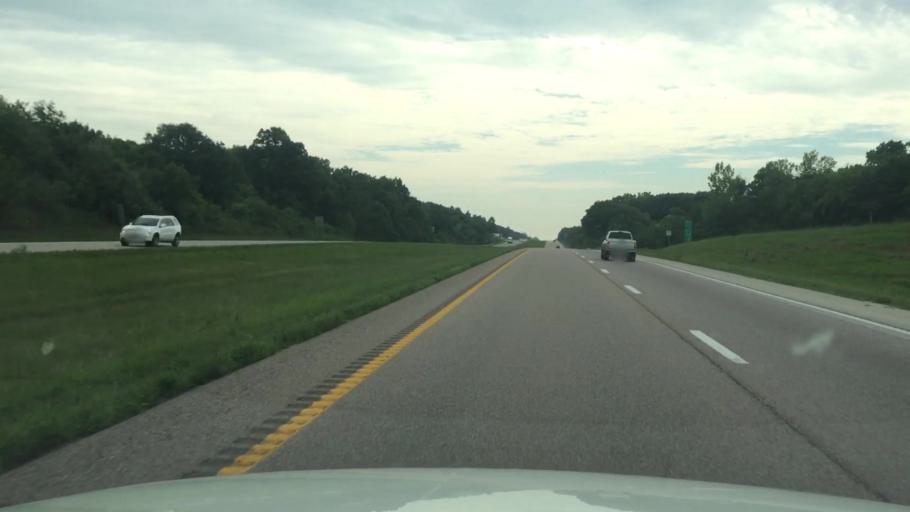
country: US
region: Missouri
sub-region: Clinton County
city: Lathrop
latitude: 39.4826
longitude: -94.3067
